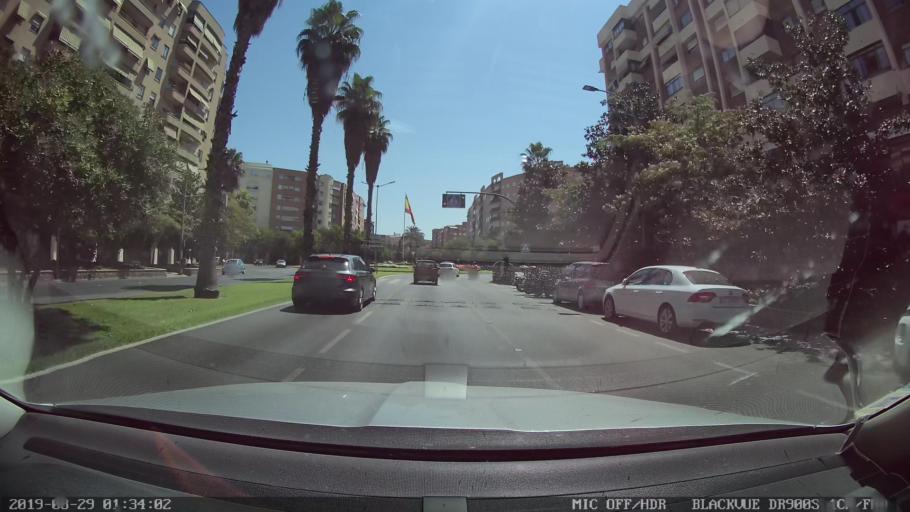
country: ES
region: Extremadura
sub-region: Provincia de Badajoz
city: Badajoz
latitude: 38.8700
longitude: -6.9885
